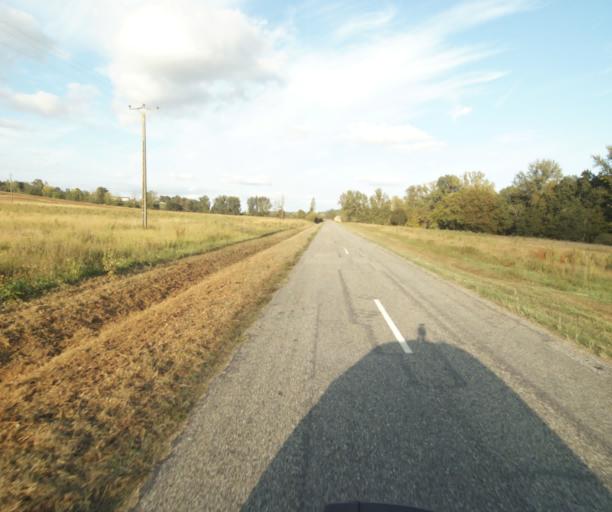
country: FR
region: Midi-Pyrenees
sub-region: Departement de la Haute-Garonne
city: Launac
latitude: 43.8139
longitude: 1.1210
